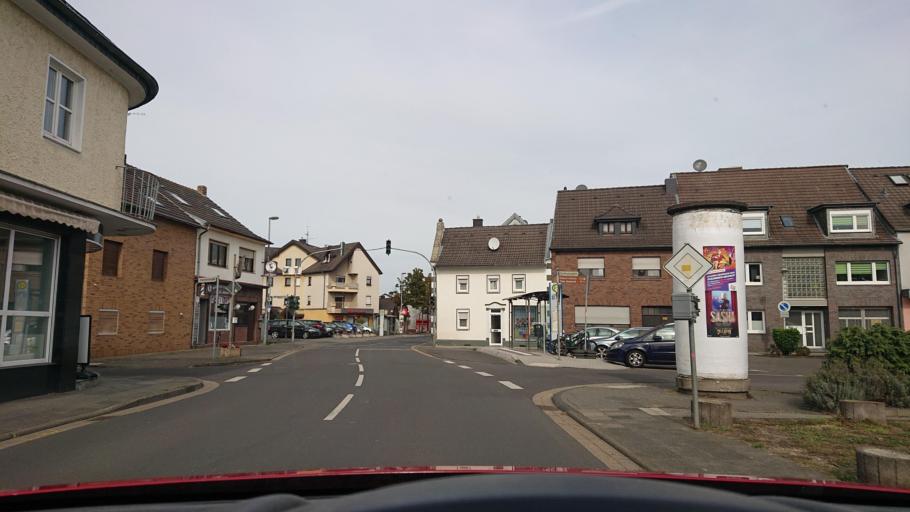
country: DE
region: North Rhine-Westphalia
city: Tuernich
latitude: 50.8360
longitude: 6.7436
